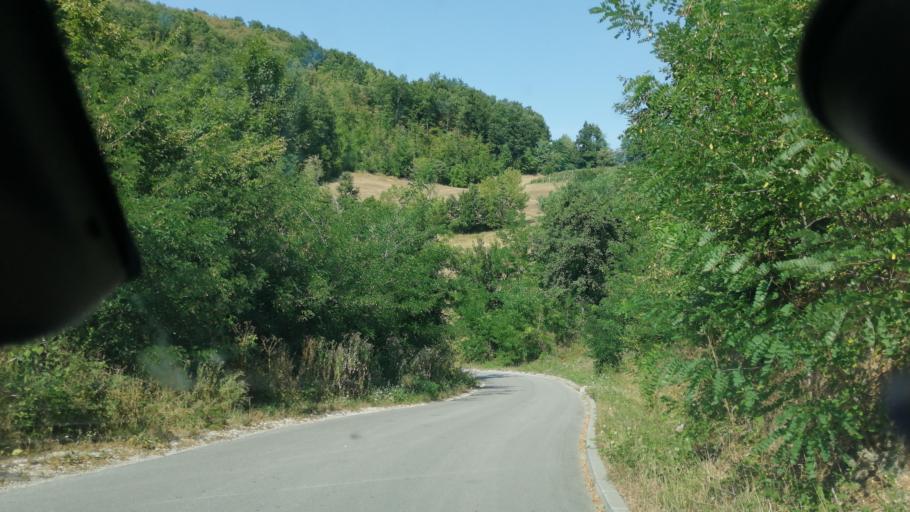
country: RS
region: Central Serbia
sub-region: Moravicki Okrug
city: Ivanjica
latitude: 43.6224
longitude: 20.2503
